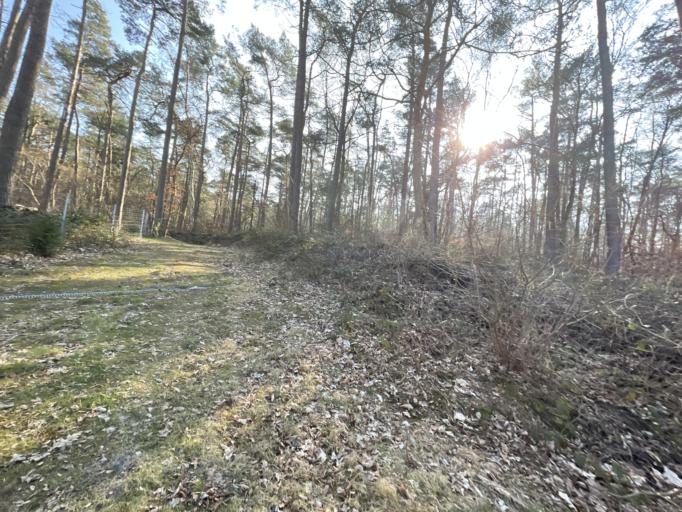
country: DE
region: Mecklenburg-Vorpommern
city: Sagard
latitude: 54.4820
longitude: 13.5602
